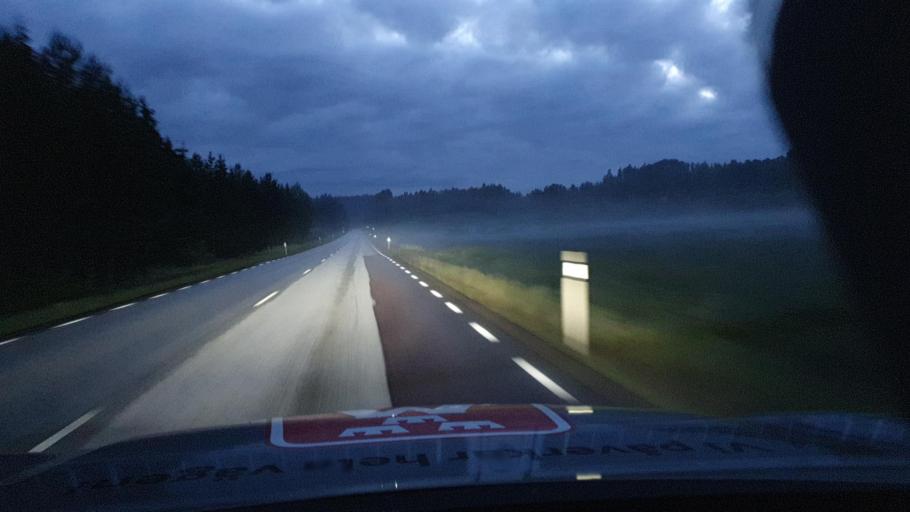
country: SE
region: Vaermland
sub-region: Storfors Kommun
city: Storfors
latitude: 59.5025
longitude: 14.3169
